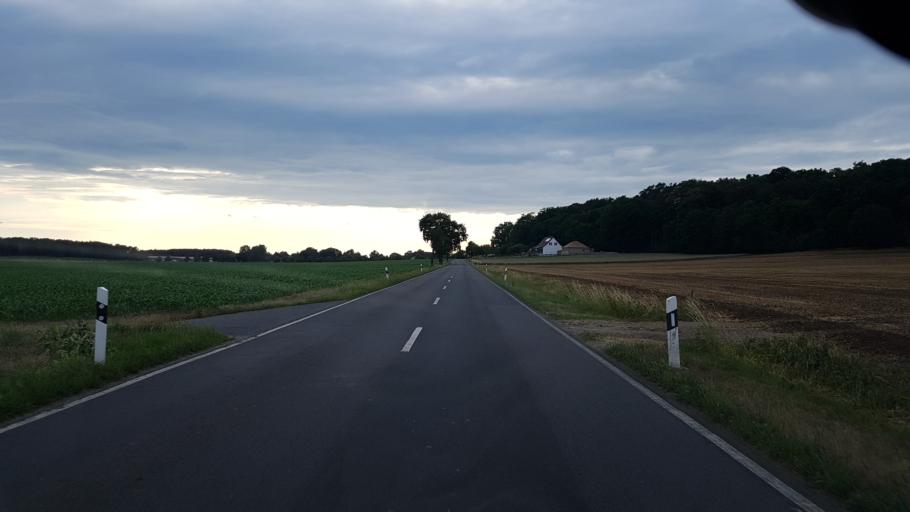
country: DE
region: Brandenburg
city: Schlieben
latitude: 51.7161
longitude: 13.3949
